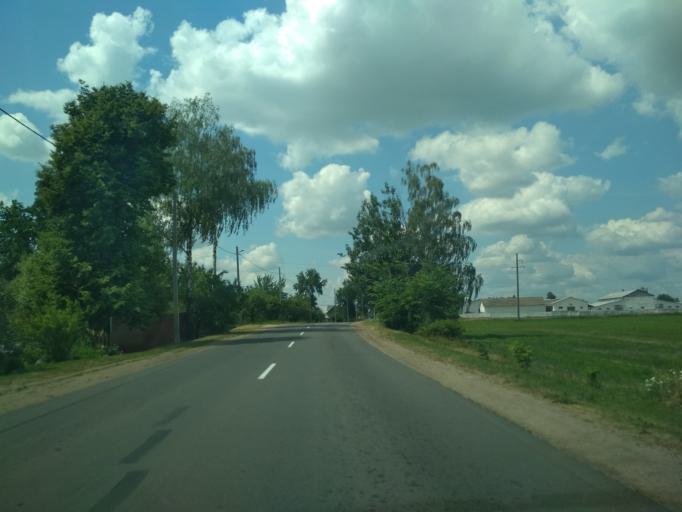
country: BY
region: Minsk
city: Svislach
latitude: 53.5701
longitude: 27.9749
